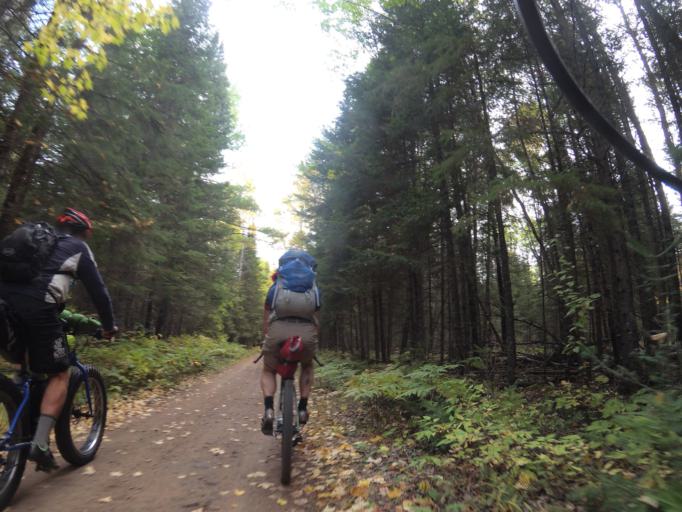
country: CA
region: Ontario
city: Pembroke
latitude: 45.2722
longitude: -77.2296
